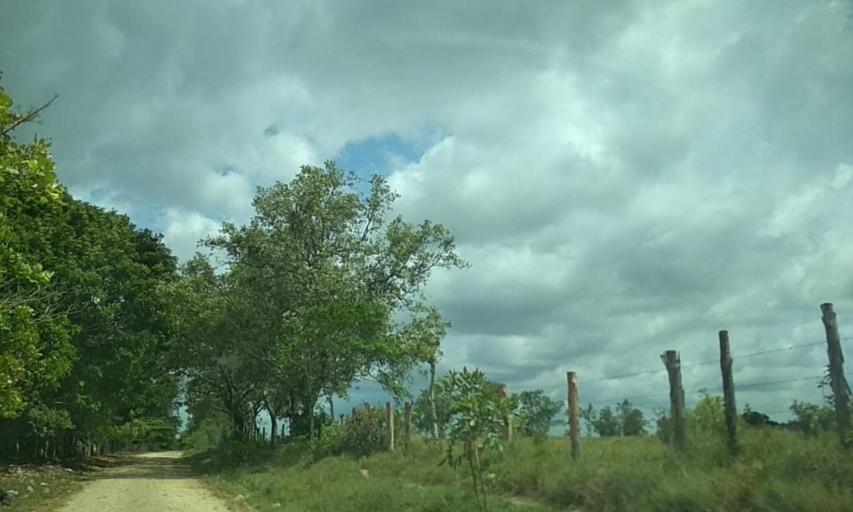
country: MX
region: Veracruz
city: Las Choapas
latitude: 17.8944
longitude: -94.1173
